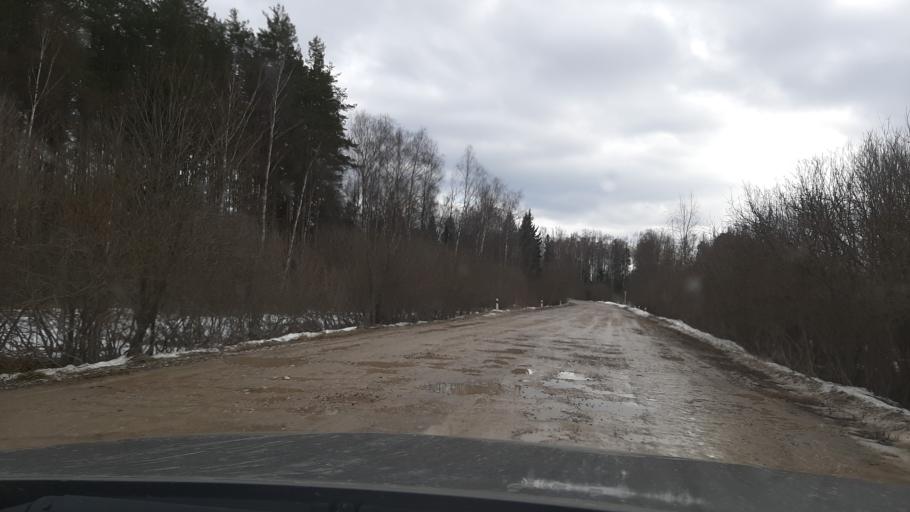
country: RU
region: Ivanovo
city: Teykovo
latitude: 56.8870
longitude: 40.6179
